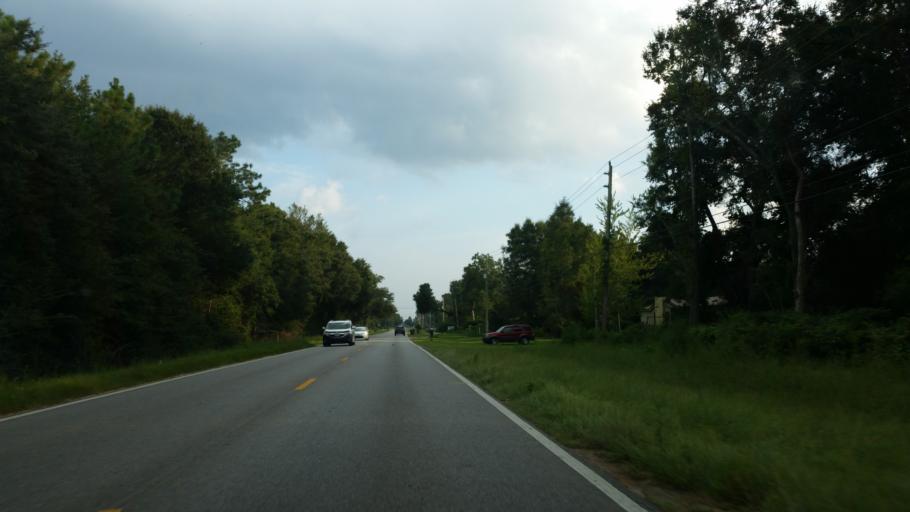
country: US
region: Florida
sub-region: Santa Rosa County
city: Pace
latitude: 30.5955
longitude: -87.1114
